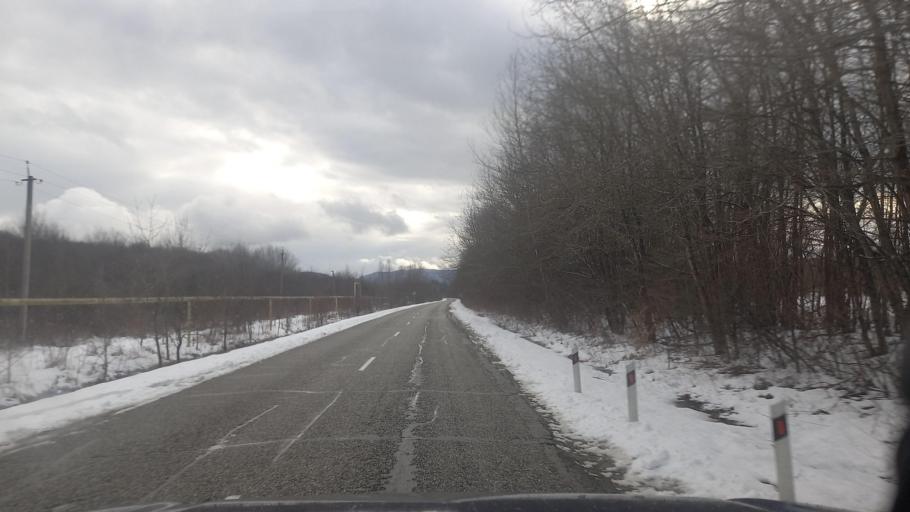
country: RU
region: Krasnodarskiy
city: Smolenskaya
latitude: 44.7454
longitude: 38.8393
